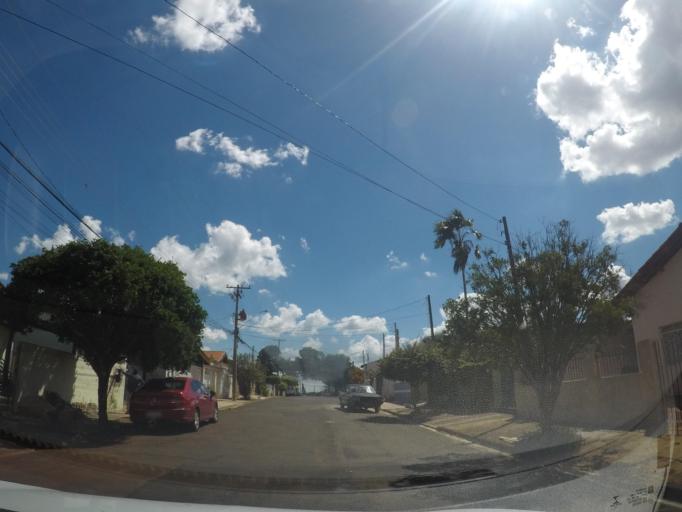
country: BR
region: Sao Paulo
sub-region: Sumare
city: Sumare
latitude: -22.8334
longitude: -47.2689
